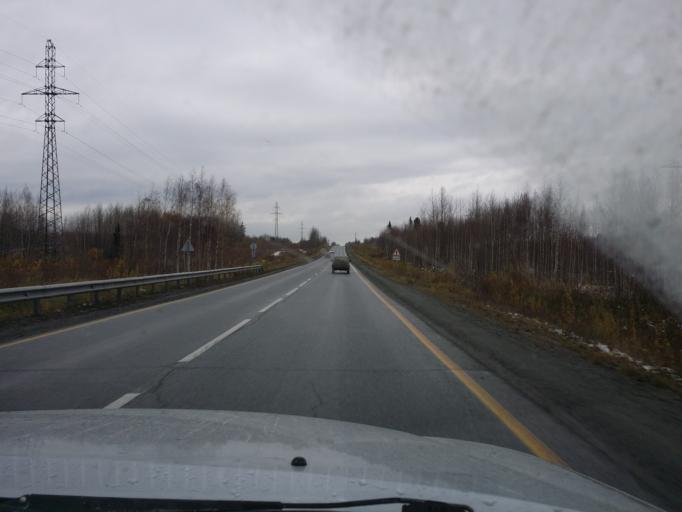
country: RU
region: Khanty-Mansiyskiy Avtonomnyy Okrug
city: Megion
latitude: 61.1021
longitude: 75.9575
